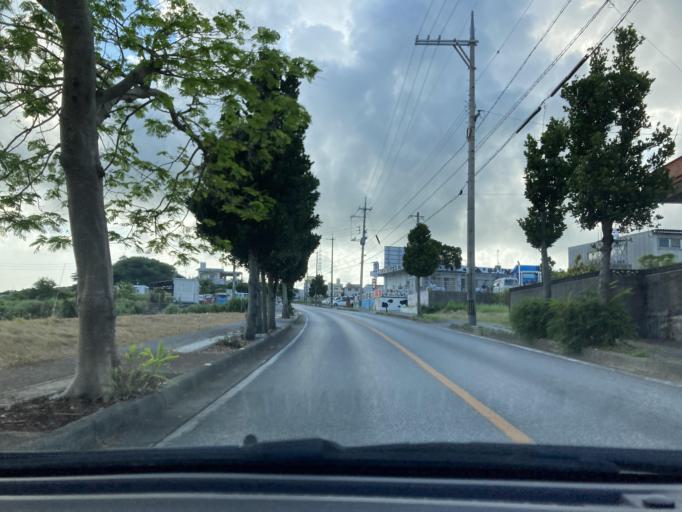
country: JP
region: Okinawa
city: Tomigusuku
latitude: 26.1749
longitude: 127.7211
